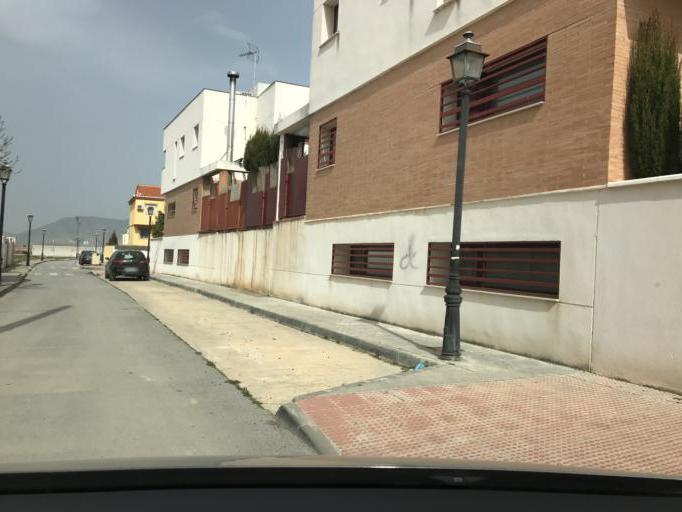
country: ES
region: Andalusia
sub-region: Provincia de Granada
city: Cullar-Vega
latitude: 37.1693
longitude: -3.6950
